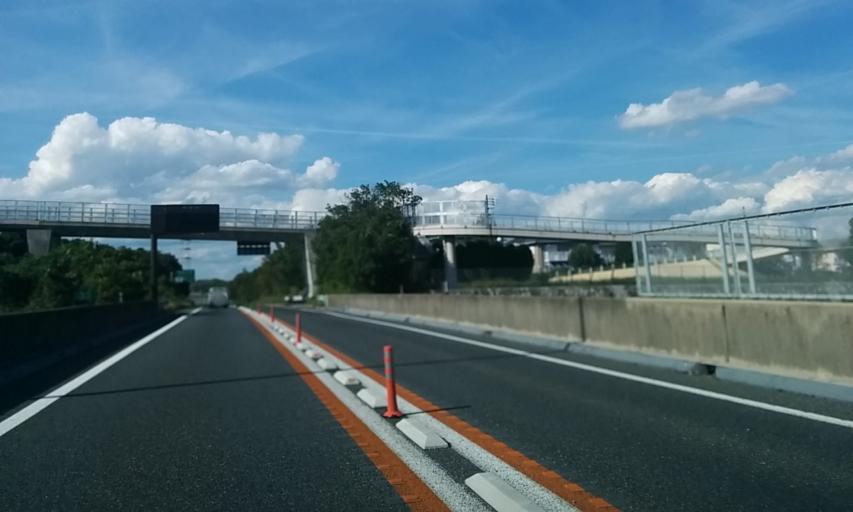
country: JP
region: Nara
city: Nara-shi
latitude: 34.7408
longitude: 135.7890
